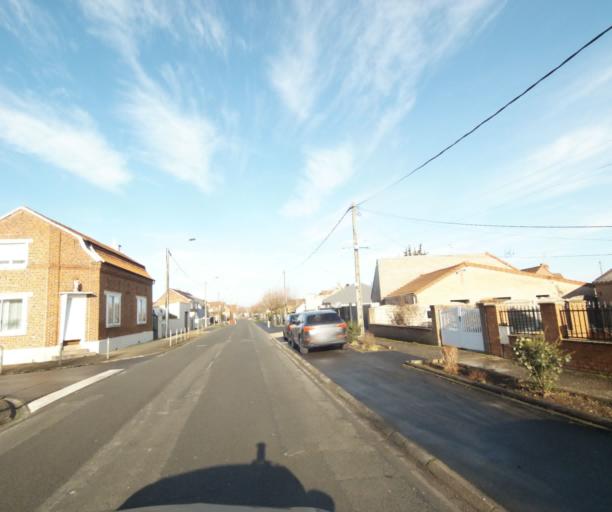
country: FR
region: Nord-Pas-de-Calais
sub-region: Departement du Nord
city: Maing
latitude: 50.3114
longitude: 3.4845
